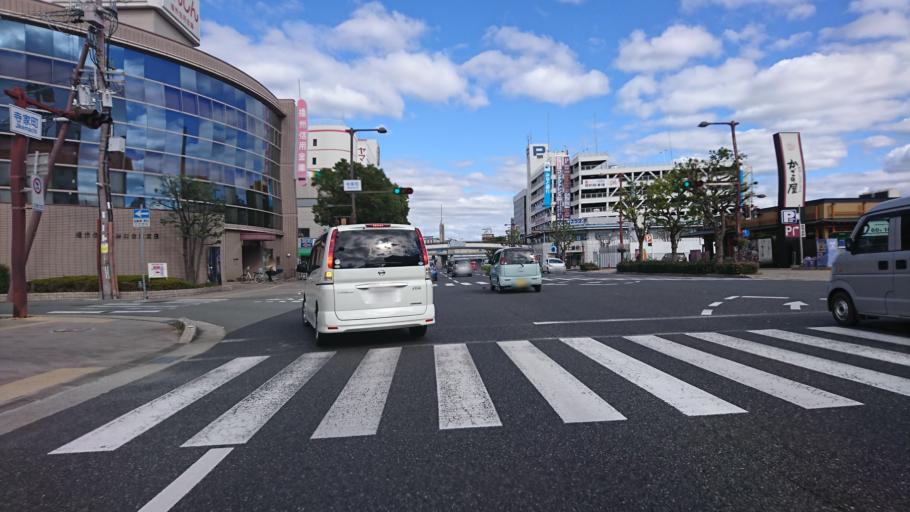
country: JP
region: Hyogo
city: Kakogawacho-honmachi
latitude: 34.7649
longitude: 134.8383
